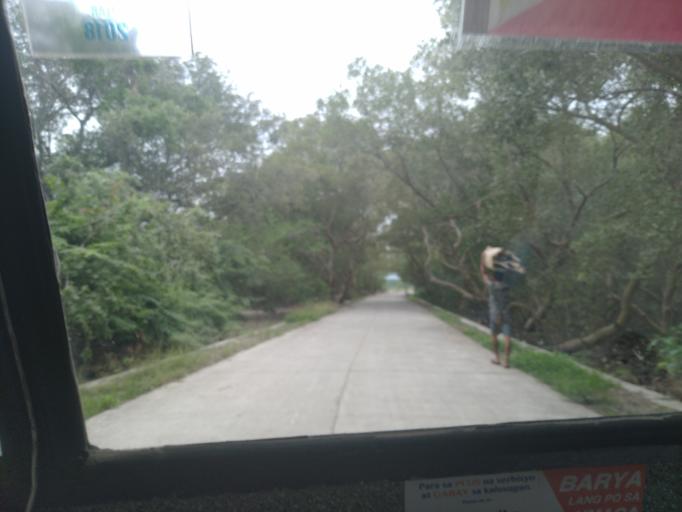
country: PH
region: Central Visayas
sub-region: Province of Negros Oriental
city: Tanjay
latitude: 9.5406
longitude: 123.1550
